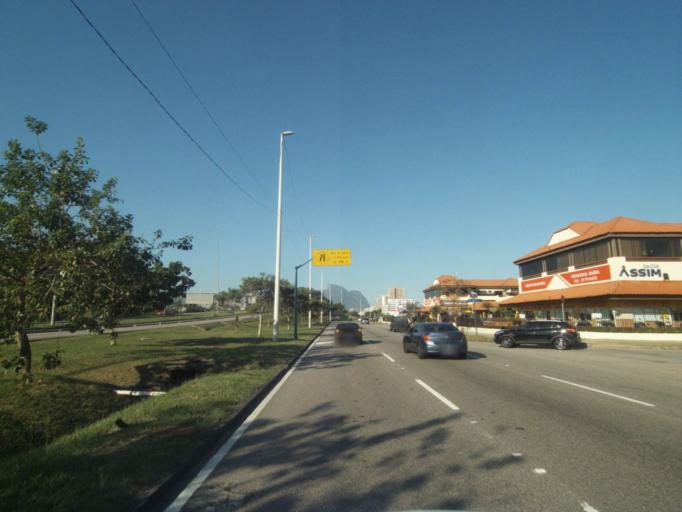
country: BR
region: Rio de Janeiro
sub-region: Rio De Janeiro
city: Rio de Janeiro
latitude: -23.0005
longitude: -43.3716
